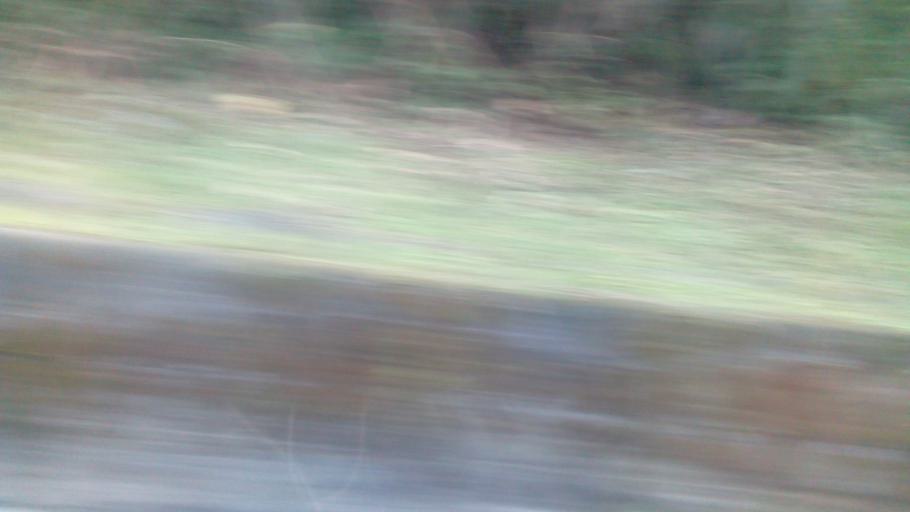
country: TW
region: Taiwan
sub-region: Yilan
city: Yilan
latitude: 24.5454
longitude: 121.4583
